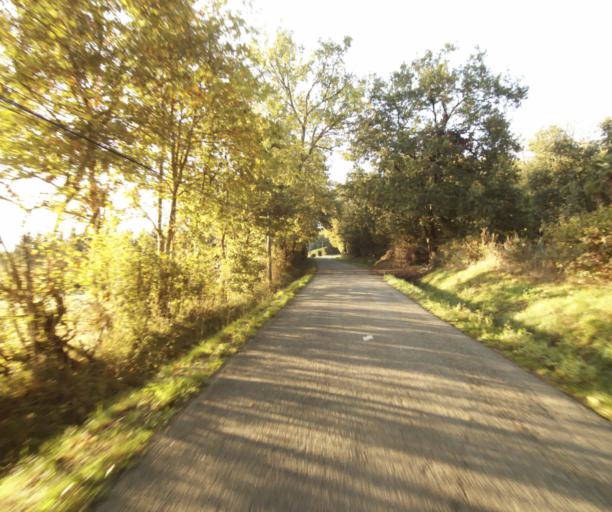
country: FR
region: Midi-Pyrenees
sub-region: Departement du Tarn-et-Garonne
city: Saint-Nauphary
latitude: 43.9393
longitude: 1.4416
